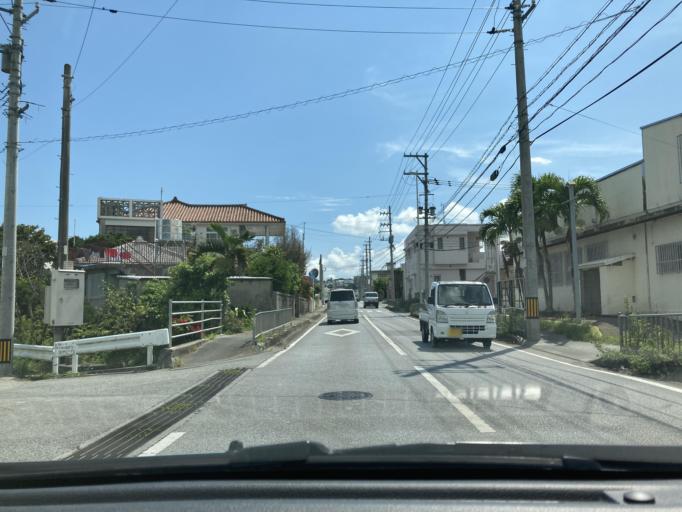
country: JP
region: Okinawa
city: Tomigusuku
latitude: 26.1823
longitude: 127.7379
